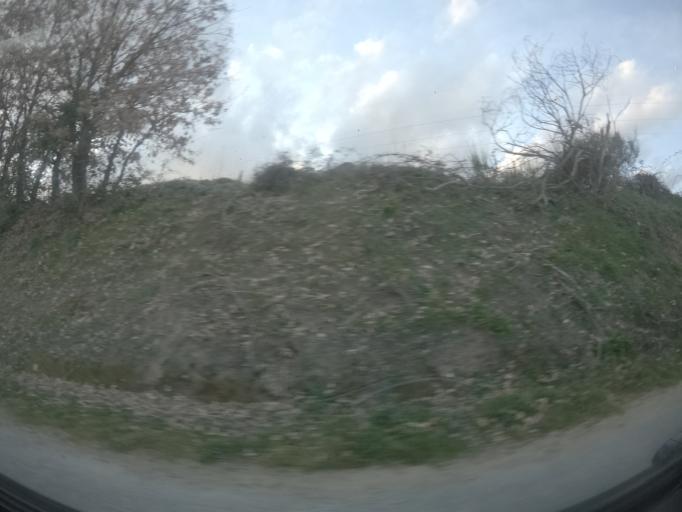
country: PT
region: Braganca
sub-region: Carrazeda de Ansiaes
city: Carrazeda de Anciaes
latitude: 41.2185
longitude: -7.3182
